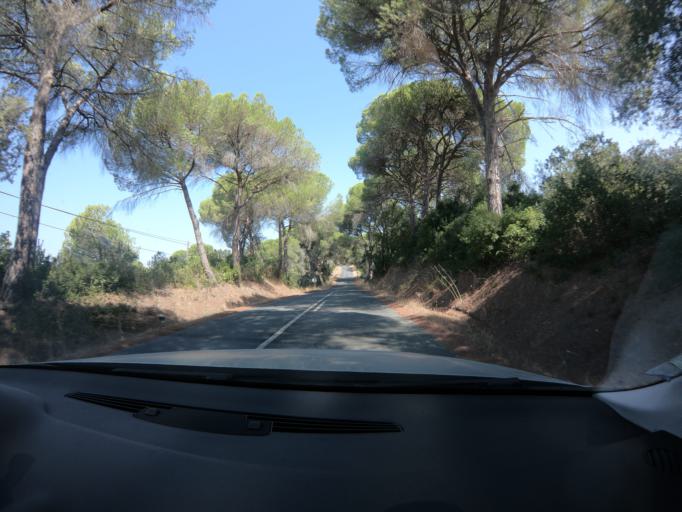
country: PT
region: Setubal
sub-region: Alcacer do Sal
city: Alcacer do Sal
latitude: 38.2957
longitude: -8.4052
